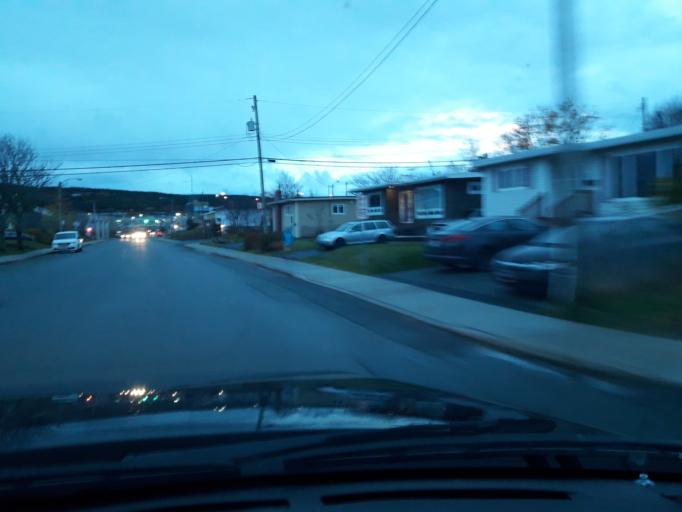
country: CA
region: Newfoundland and Labrador
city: St. John's
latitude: 47.5640
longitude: -52.7547
